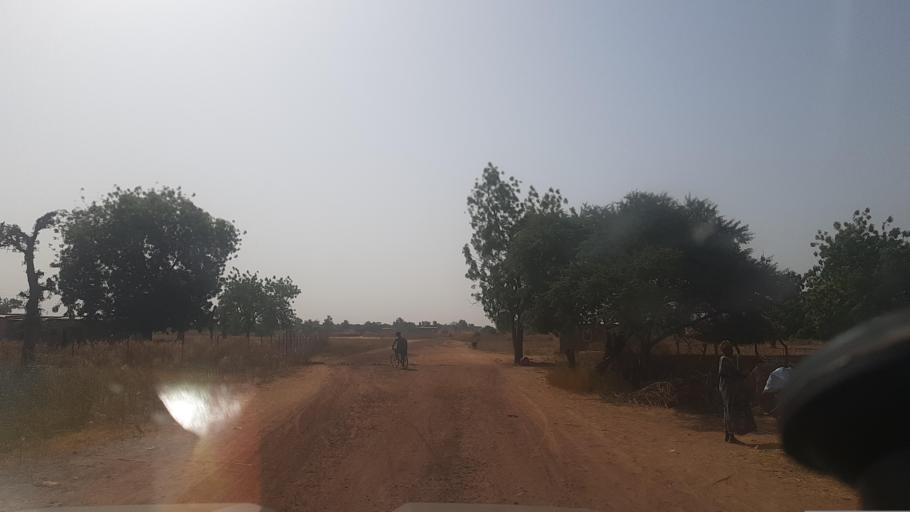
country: ML
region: Segou
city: Baroueli
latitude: 13.1641
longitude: -6.5182
